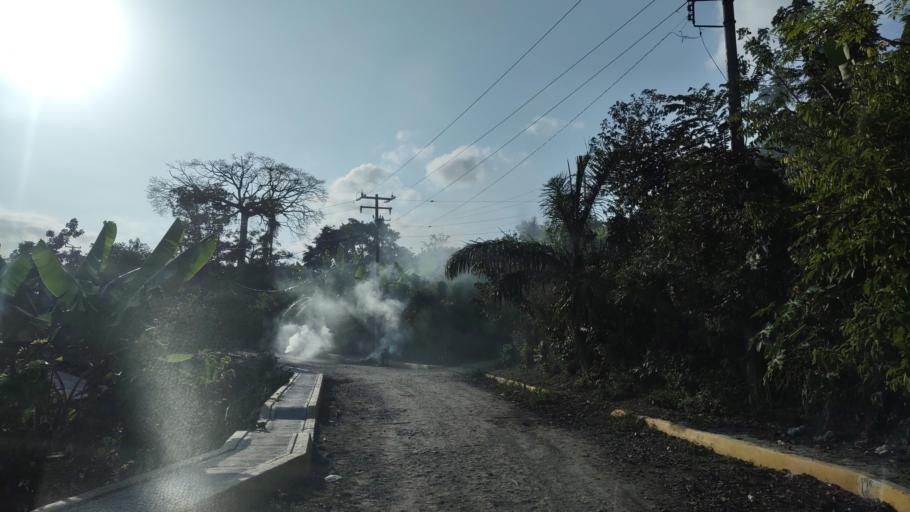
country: MX
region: Veracruz
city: Papantla de Olarte
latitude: 20.4611
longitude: -97.3631
